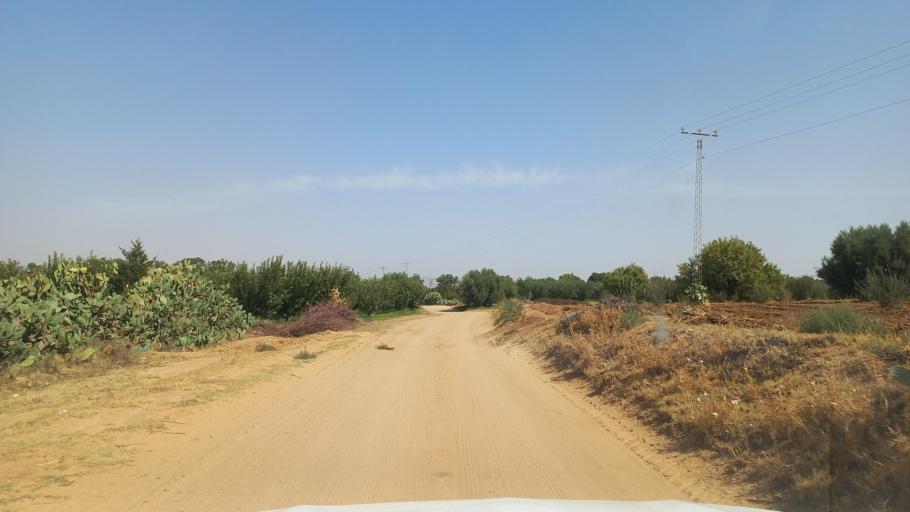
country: TN
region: Al Qasrayn
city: Kasserine
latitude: 35.2574
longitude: 9.0436
